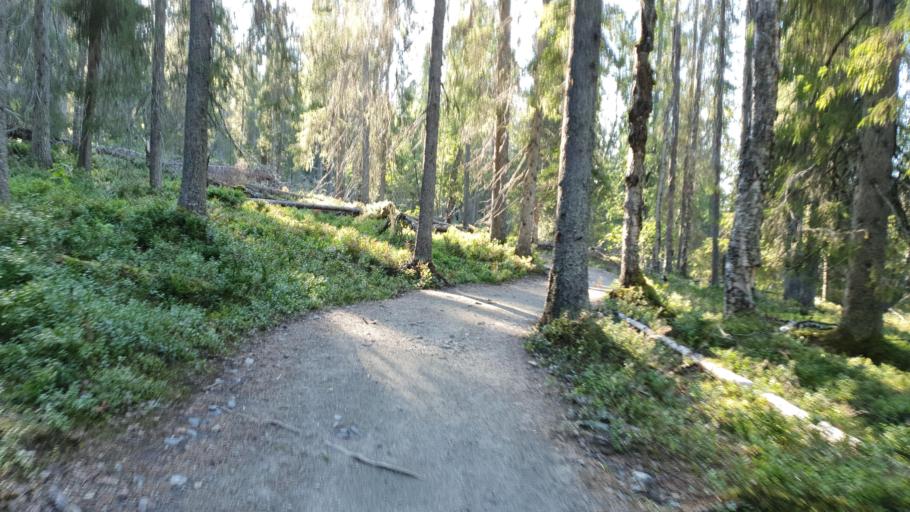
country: FI
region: Lapland
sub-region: Tunturi-Lappi
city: Kolari
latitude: 67.5966
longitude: 24.2300
